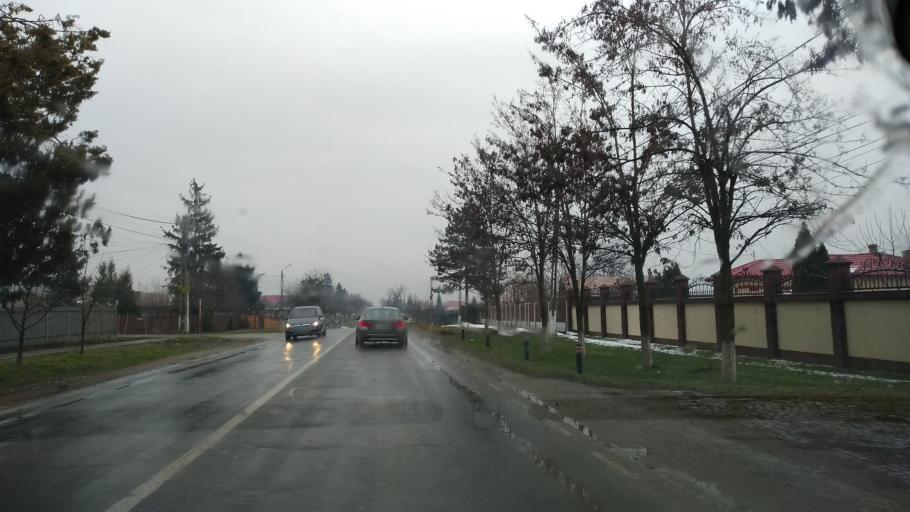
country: RO
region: Calarasi
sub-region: Comuna Frumusani
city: Frumusani
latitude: 44.2989
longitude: 26.3089
